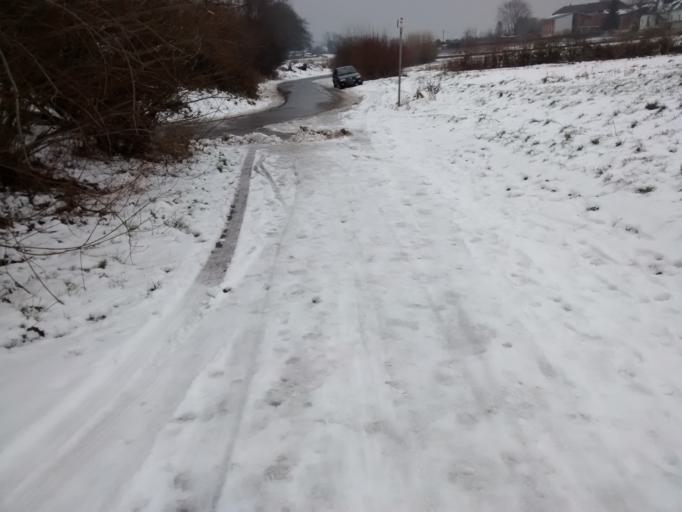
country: NL
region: Limburg
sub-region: Gemeente Vaals
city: Vaals
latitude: 50.7652
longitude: 6.0454
